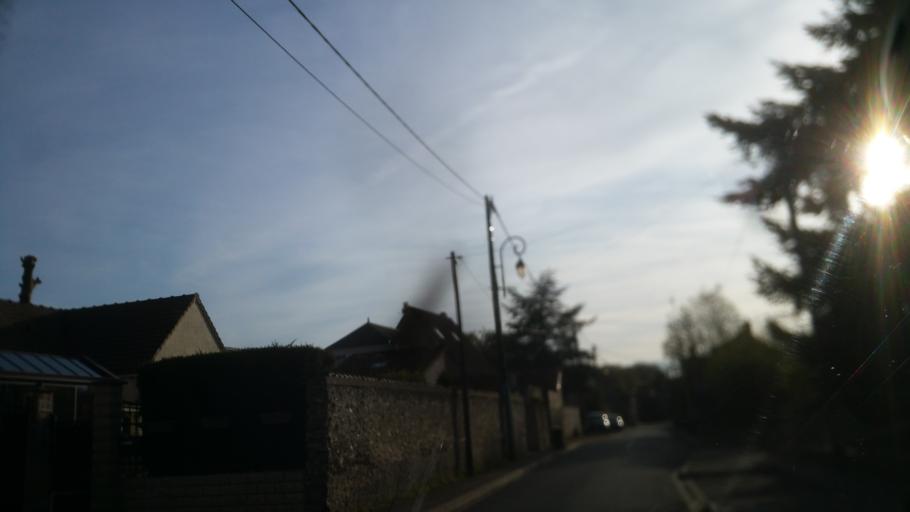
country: FR
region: Ile-de-France
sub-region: Departement de l'Essonne
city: Le Val-Saint-Germain
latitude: 48.5658
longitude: 2.0655
